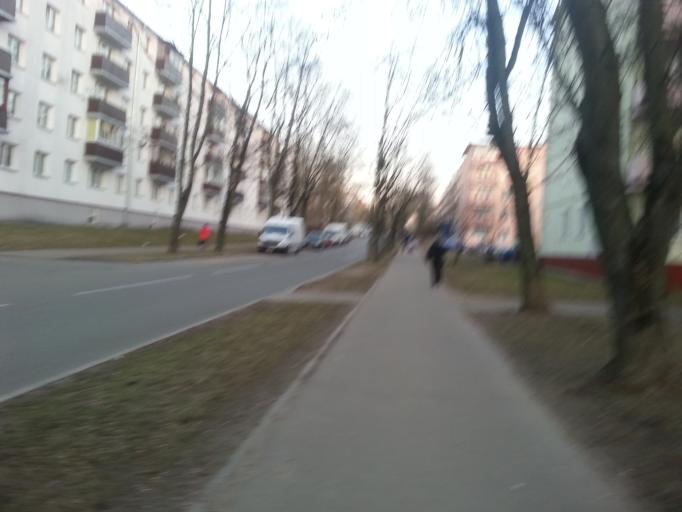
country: BY
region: Minsk
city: Minsk
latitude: 53.8743
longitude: 27.6184
